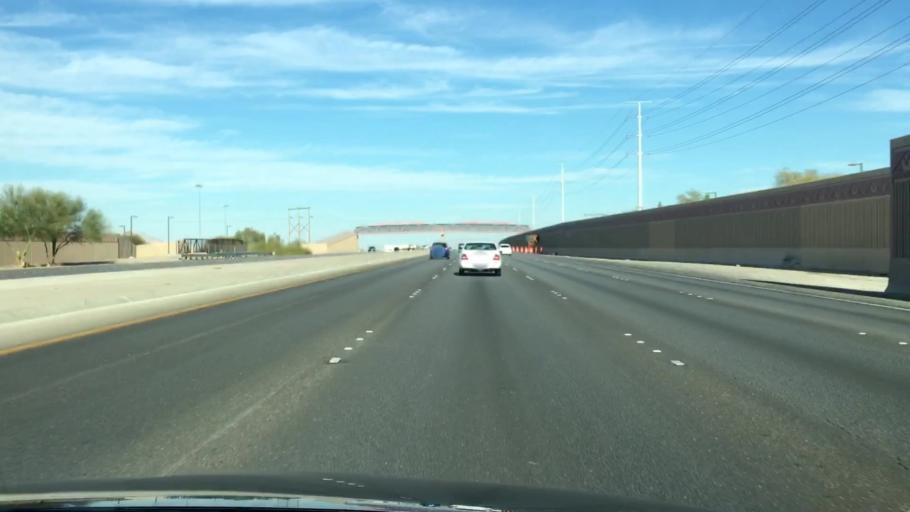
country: US
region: Nevada
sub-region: Clark County
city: Whitney
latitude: 36.0105
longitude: -115.1095
